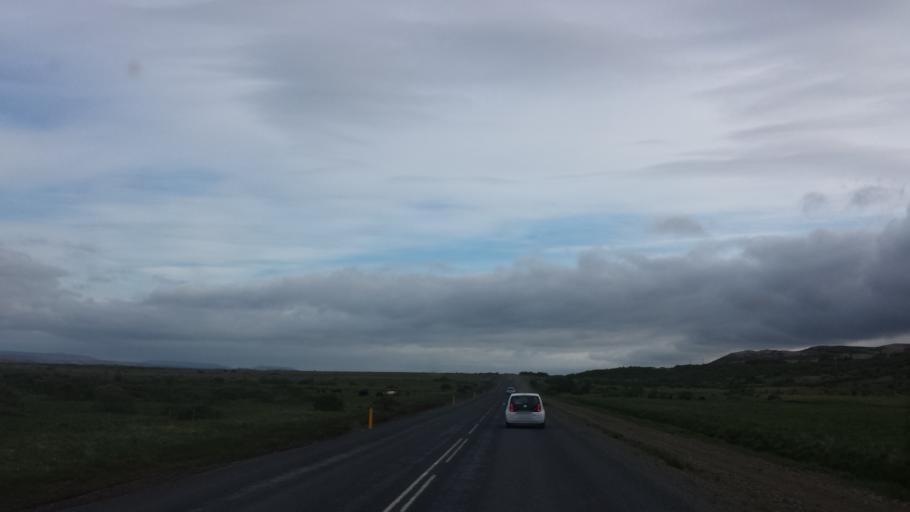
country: IS
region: South
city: Selfoss
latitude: 64.2946
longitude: -20.3350
